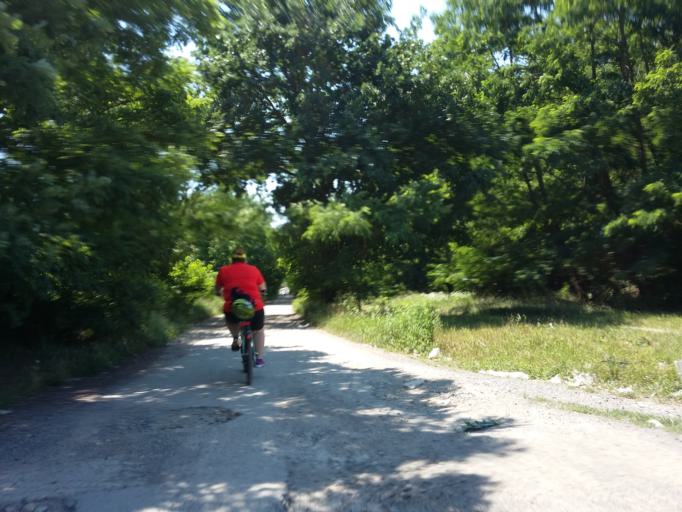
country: AT
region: Lower Austria
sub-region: Politischer Bezirk Ganserndorf
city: Marchegg
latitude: 48.2760
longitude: 16.9658
